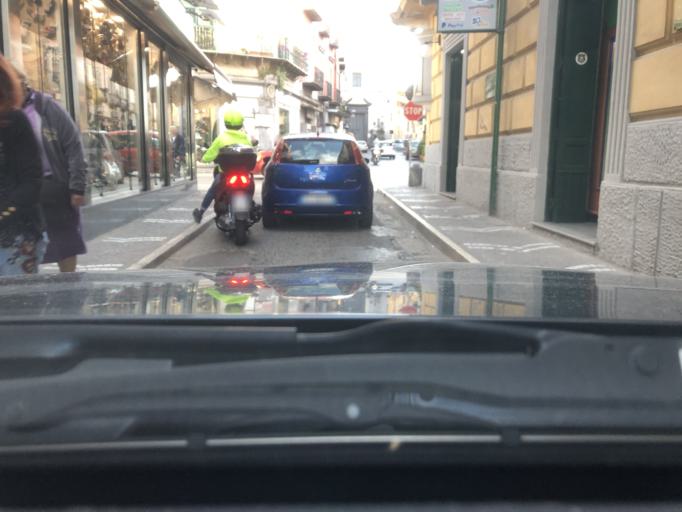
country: IT
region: Campania
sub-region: Provincia di Napoli
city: Calvizzano
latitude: 40.8987
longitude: 14.1888
